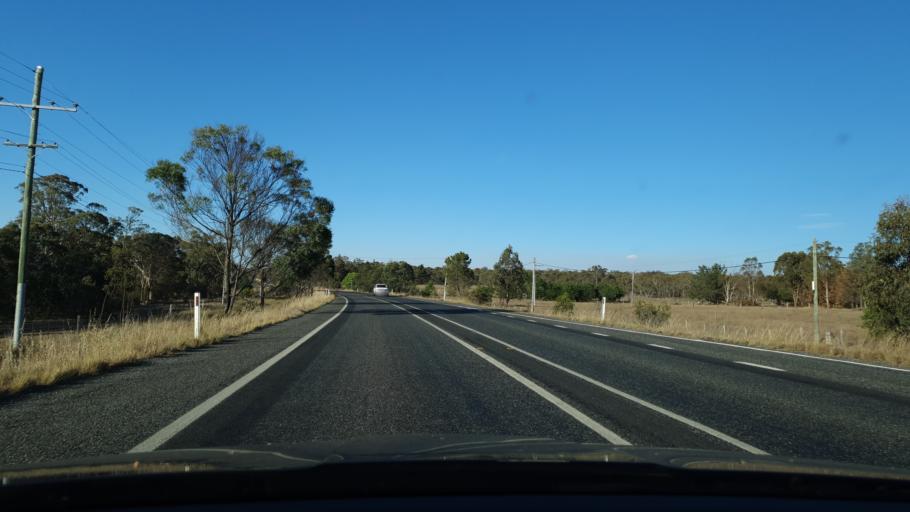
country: AU
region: Queensland
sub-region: Southern Downs
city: Stanthorpe
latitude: -28.7019
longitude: 151.9045
